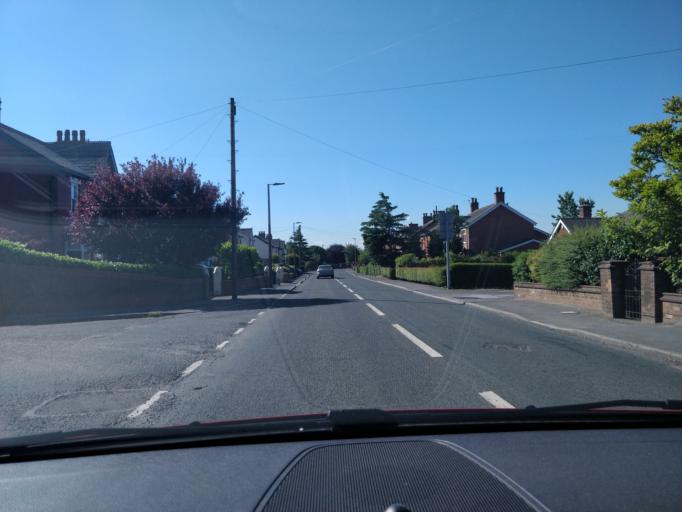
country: GB
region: England
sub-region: Lancashire
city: Tarleton
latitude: 53.6845
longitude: -2.8314
